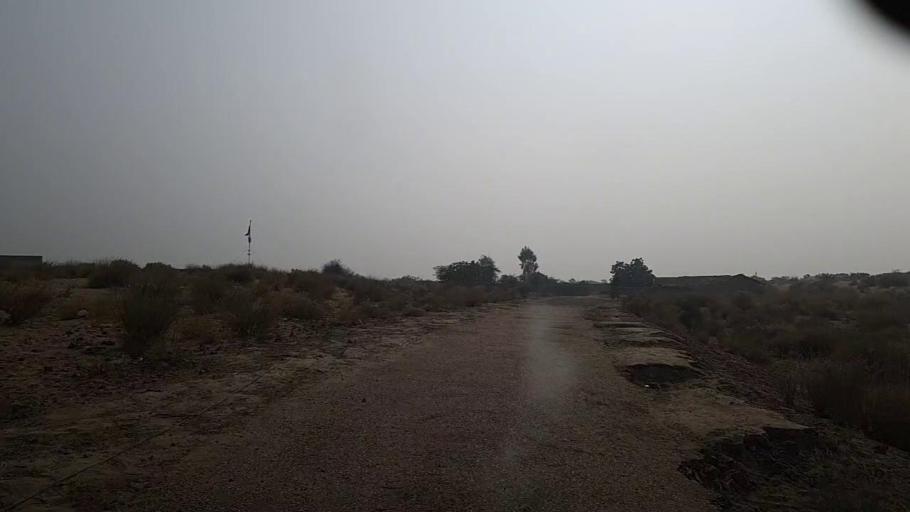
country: PK
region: Sindh
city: Bozdar
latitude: 27.0665
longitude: 68.6321
